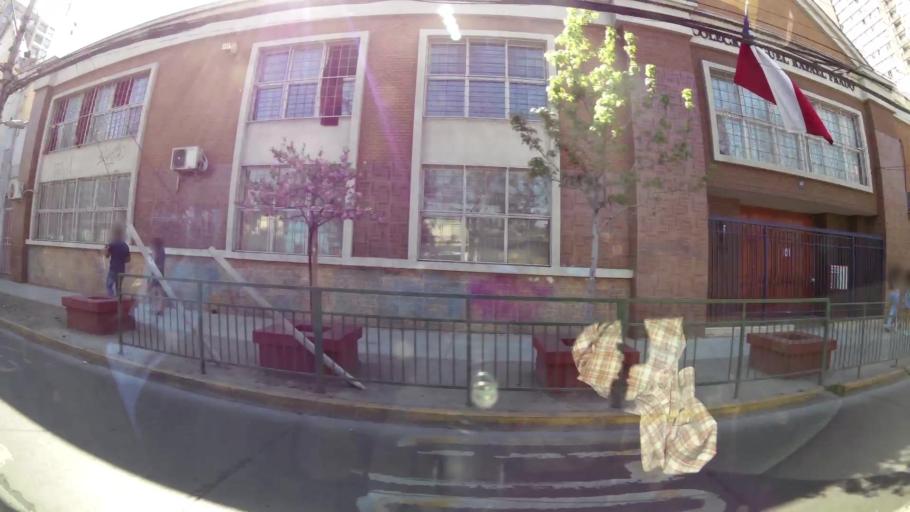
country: CL
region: Santiago Metropolitan
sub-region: Provincia de Santiago
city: Santiago
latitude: -33.4215
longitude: -70.6623
